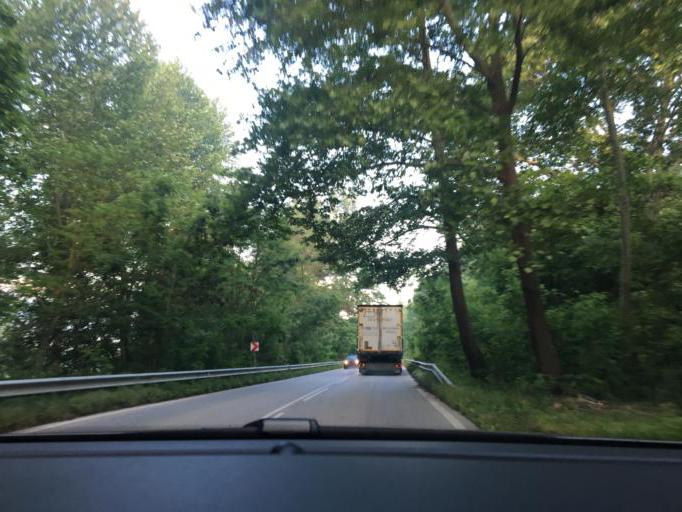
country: BG
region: Blagoevgrad
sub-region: Obshtina Petrich
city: Petrich
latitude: 41.3994
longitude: 23.0741
